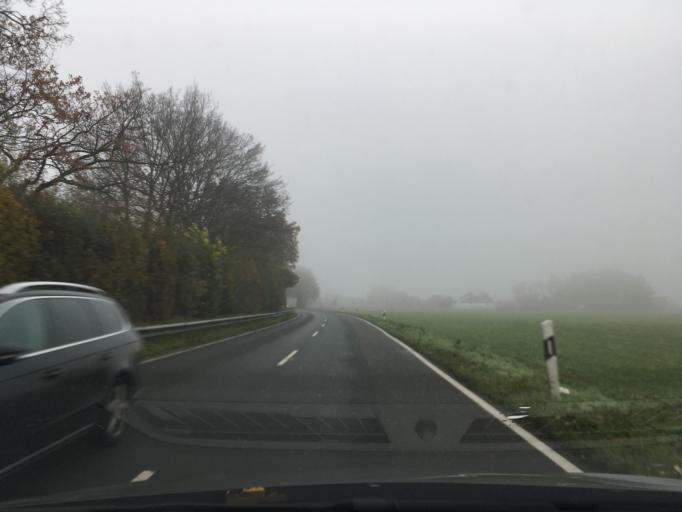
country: DE
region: North Rhine-Westphalia
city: Stadtlohn
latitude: 52.0712
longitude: 6.9270
